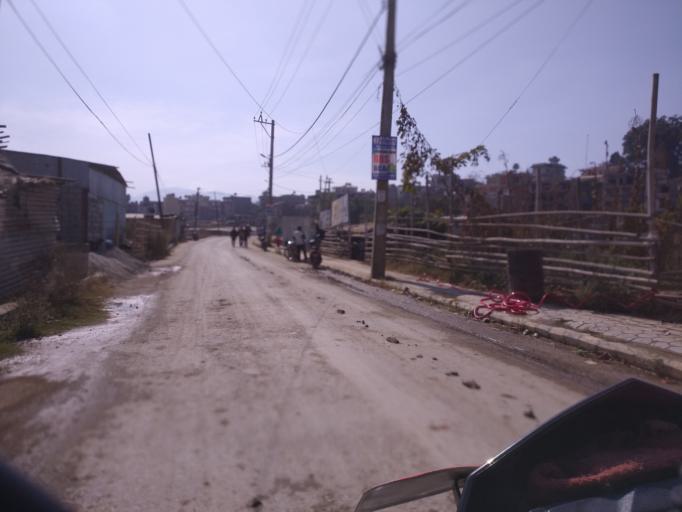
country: NP
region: Central Region
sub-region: Bagmati Zone
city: Patan
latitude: 27.6515
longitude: 85.3131
